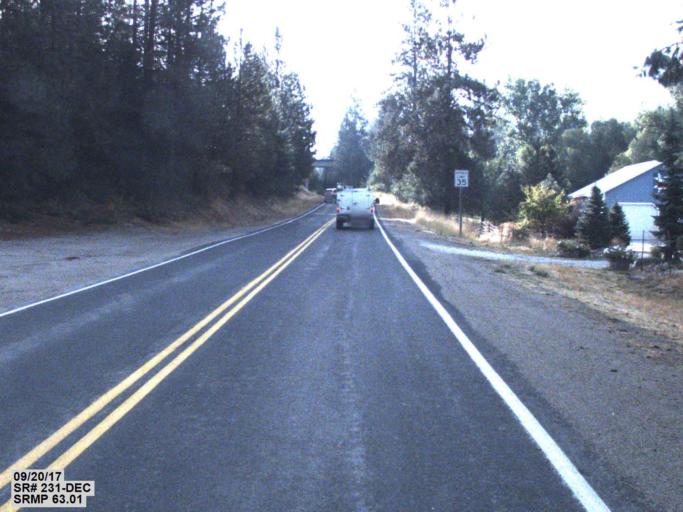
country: US
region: Washington
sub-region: Stevens County
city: Chewelah
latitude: 48.0593
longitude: -117.7559
